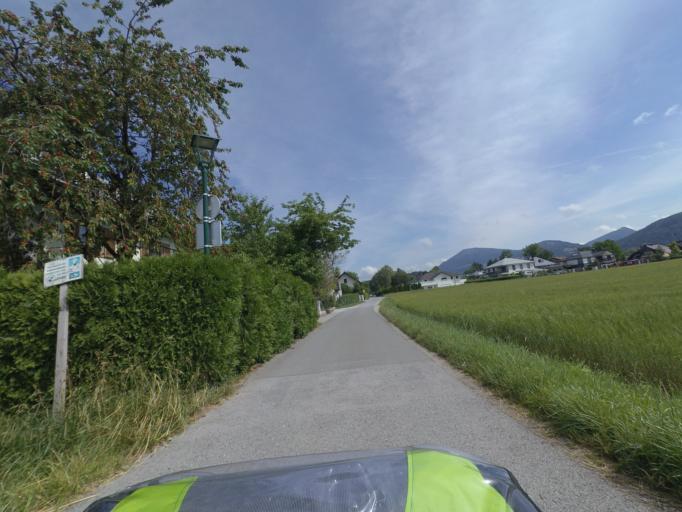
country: AT
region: Salzburg
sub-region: Politischer Bezirk Salzburg-Umgebung
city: Anif
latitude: 47.7430
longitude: 13.0618
